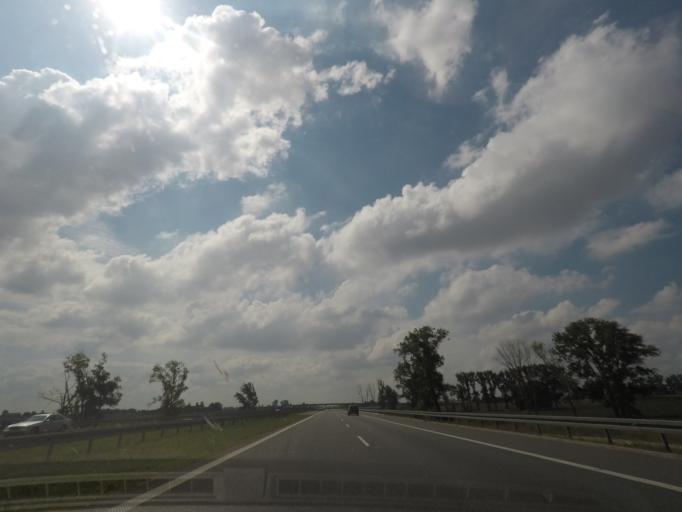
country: PL
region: Lodz Voivodeship
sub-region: Powiat kutnowski
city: Krzyzanow
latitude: 52.1749
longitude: 19.4856
